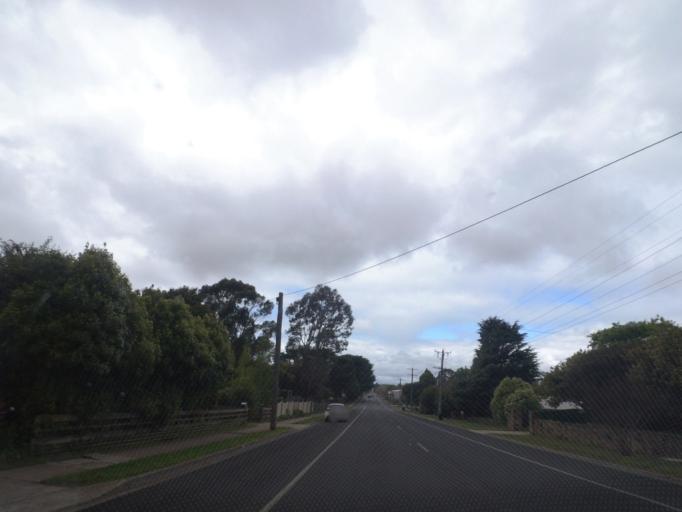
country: AU
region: Victoria
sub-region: Hume
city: Sunbury
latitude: -37.3507
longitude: 144.7398
